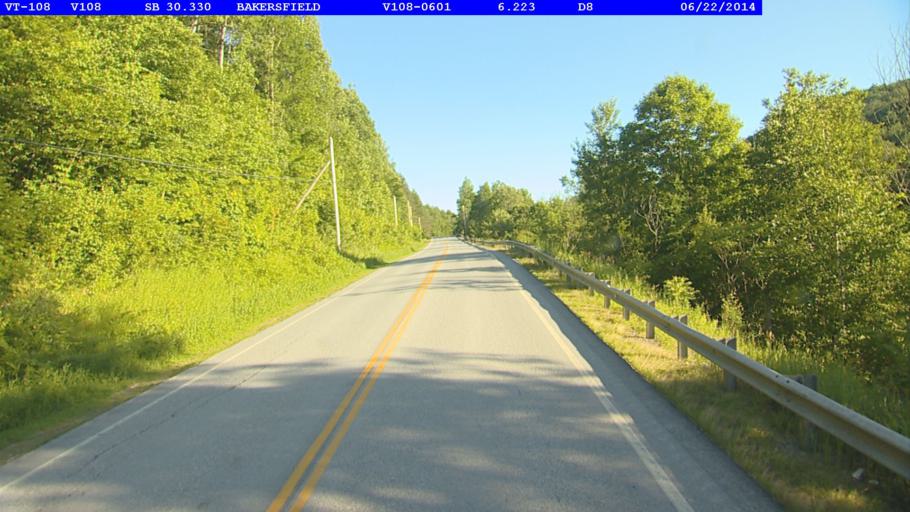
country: US
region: Vermont
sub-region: Franklin County
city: Enosburg Falls
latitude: 44.8159
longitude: -72.7906
